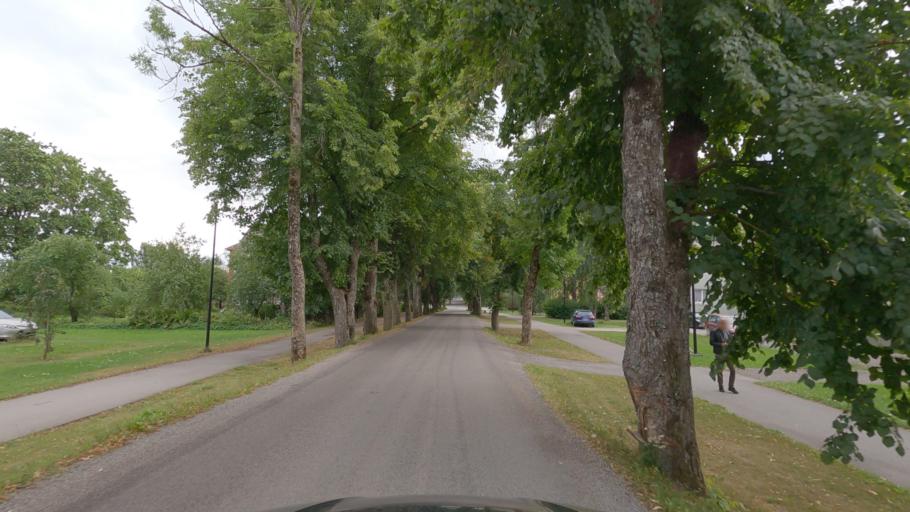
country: EE
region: Raplamaa
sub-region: Kohila vald
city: Kohila
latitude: 59.1726
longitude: 24.7502
